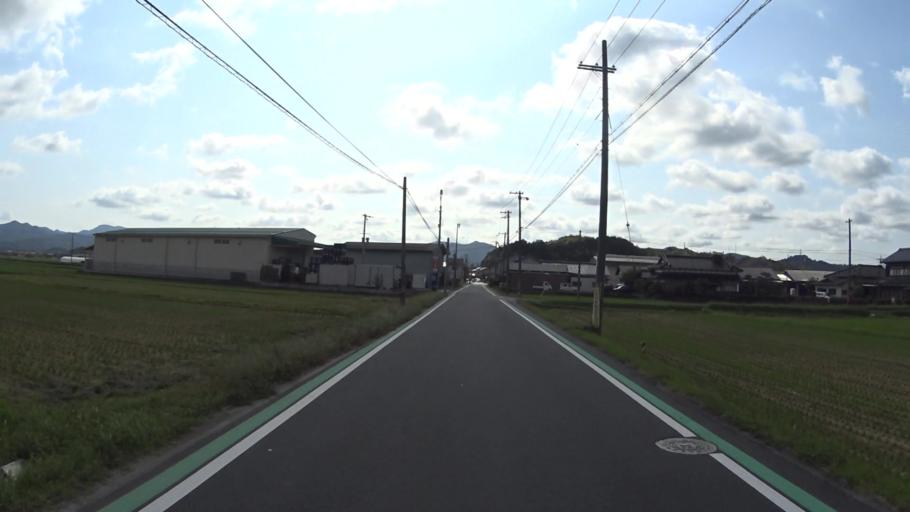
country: JP
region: Kyoto
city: Miyazu
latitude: 35.6317
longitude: 135.0773
